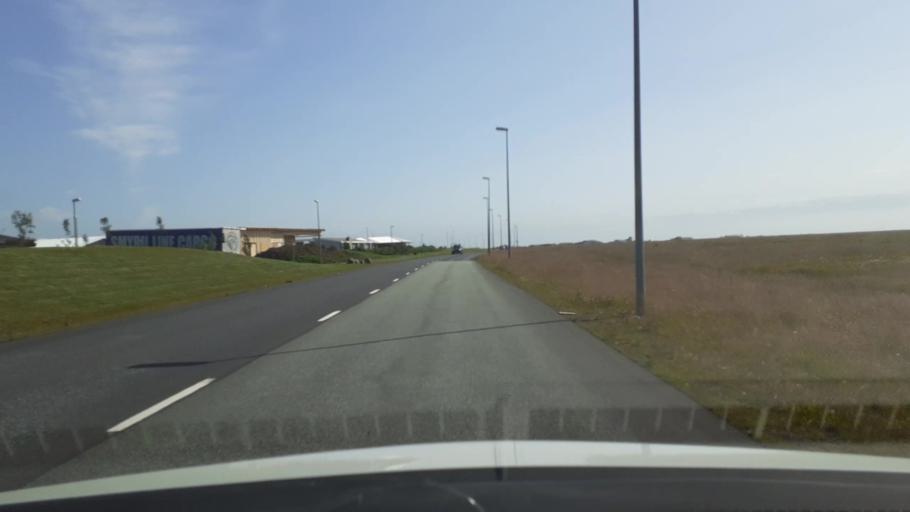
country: IS
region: South
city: Selfoss
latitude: 63.9261
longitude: -21.0150
